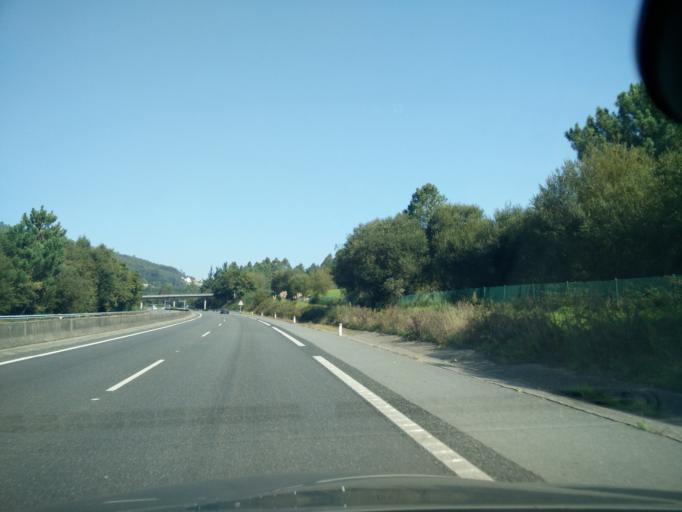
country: ES
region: Galicia
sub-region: Provincia da Coruna
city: Mino
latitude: 43.3851
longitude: -8.1776
